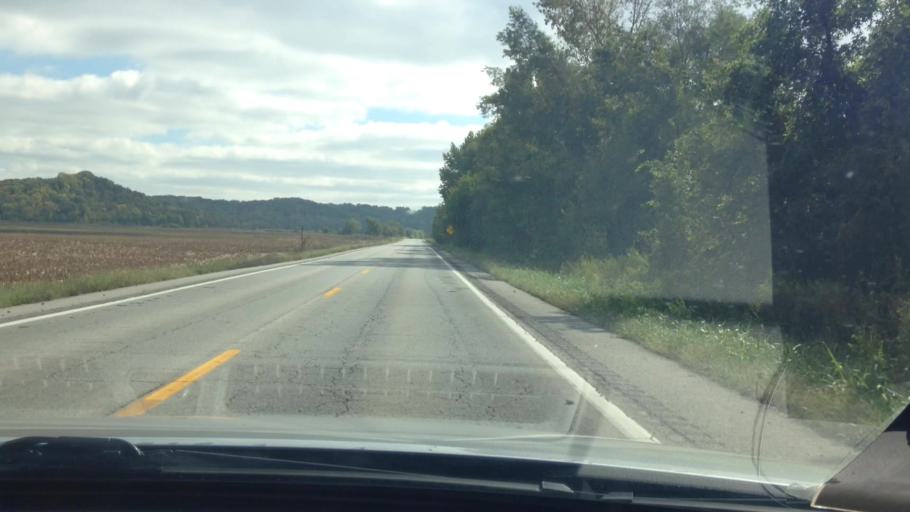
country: US
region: Kansas
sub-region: Leavenworth County
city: Lansing
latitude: 39.2657
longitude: -94.8177
